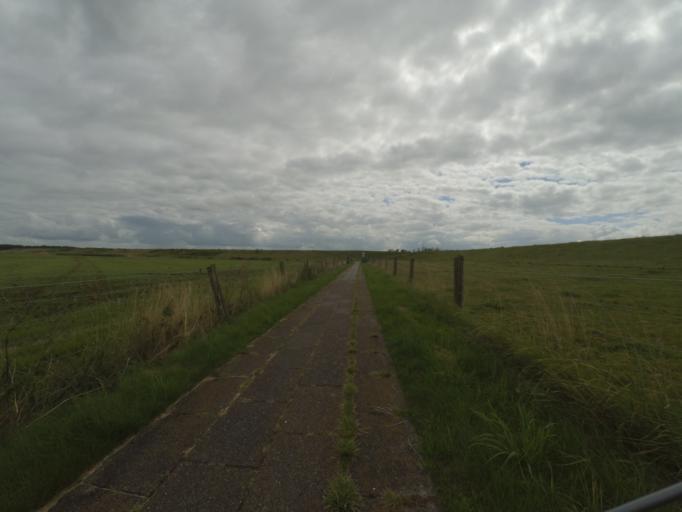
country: NL
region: Friesland
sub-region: Gemeente Dongeradeel
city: Anjum
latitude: 53.3369
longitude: 6.1545
